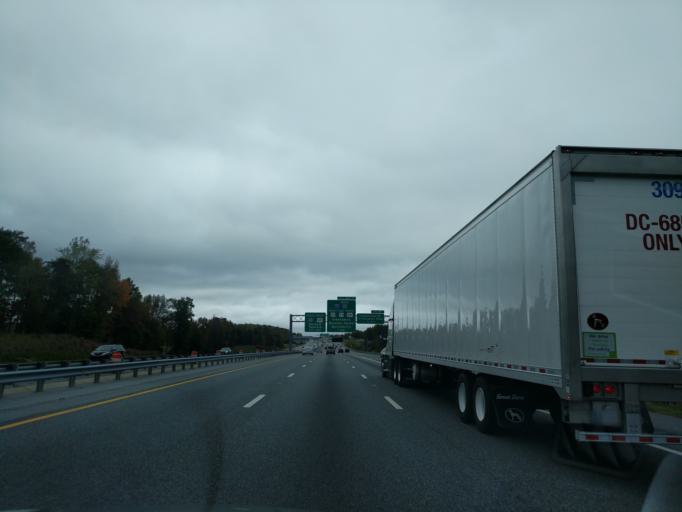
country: US
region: North Carolina
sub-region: Guilford County
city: Jamestown
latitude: 35.9894
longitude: -79.8771
